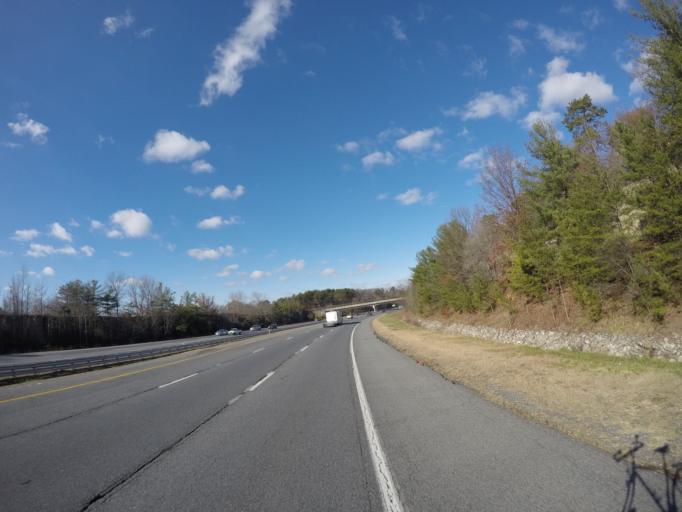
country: US
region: Maryland
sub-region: Anne Arundel County
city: South Gate
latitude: 39.1427
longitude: -76.5976
